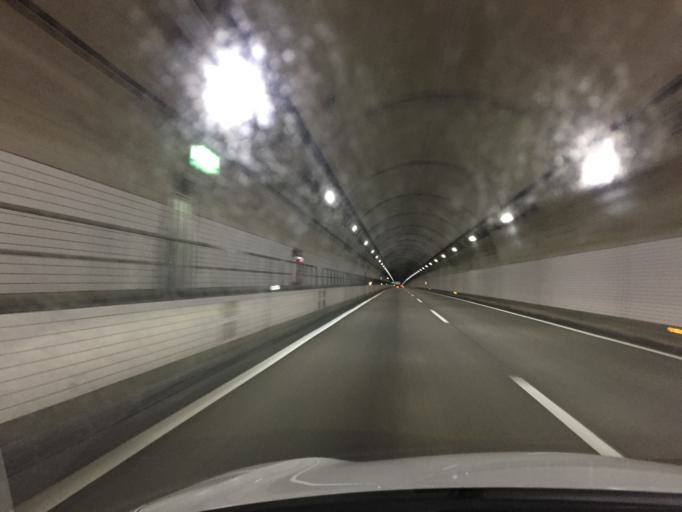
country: JP
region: Ibaraki
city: Kitaibaraki
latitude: 36.8356
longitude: 140.7315
